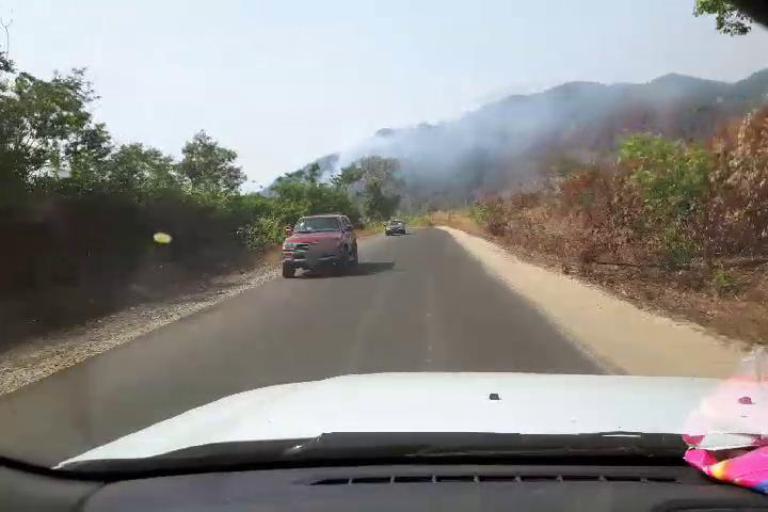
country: SL
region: Western Area
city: Waterloo
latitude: 8.2512
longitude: -13.1541
